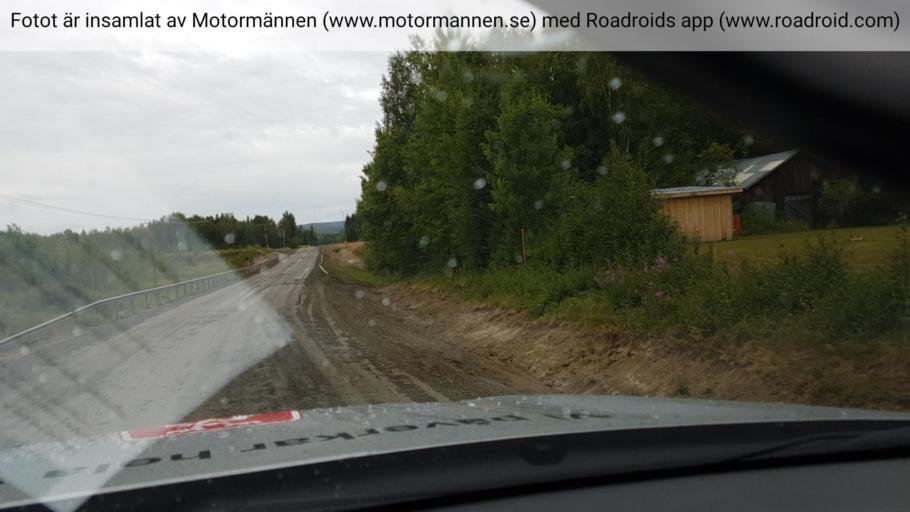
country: SE
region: Norrbotten
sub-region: Alvsbyns Kommun
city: AElvsbyn
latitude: 65.9090
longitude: 21.2884
